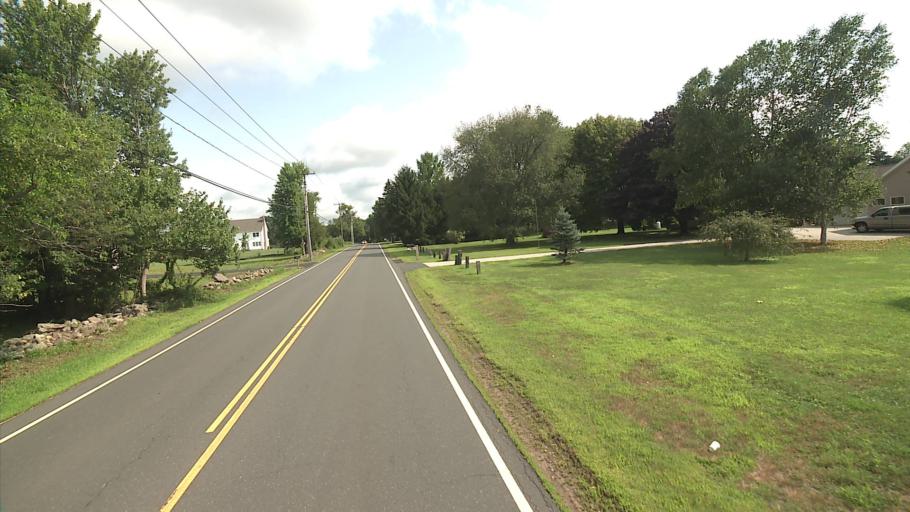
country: US
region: Connecticut
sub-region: Middlesex County
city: Moodus
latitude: 41.5328
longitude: -72.4115
